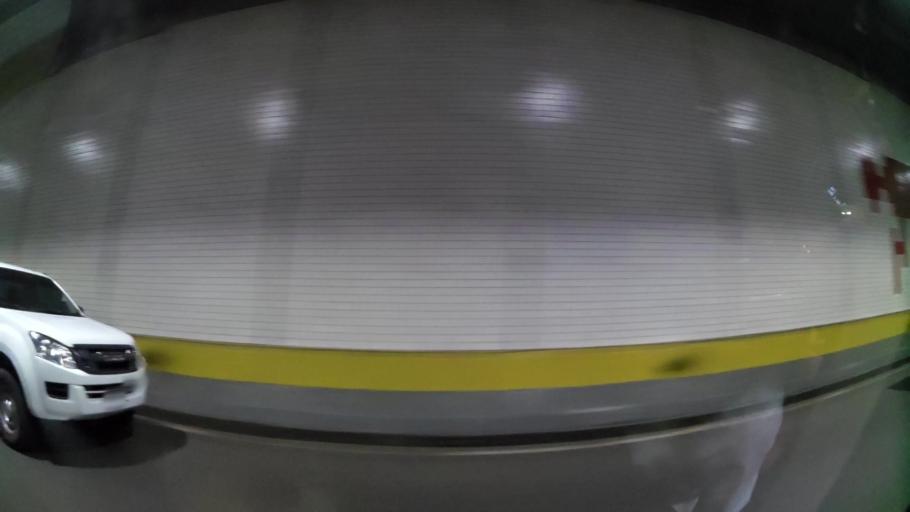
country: DO
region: Santo Domingo
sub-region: Santo Domingo
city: Santo Domingo Este
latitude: 18.4852
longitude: -69.8700
